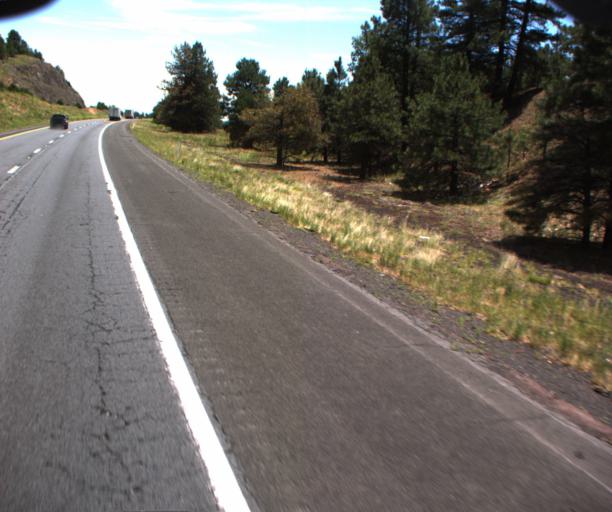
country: US
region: Arizona
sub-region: Coconino County
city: Parks
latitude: 35.2511
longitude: -111.8982
